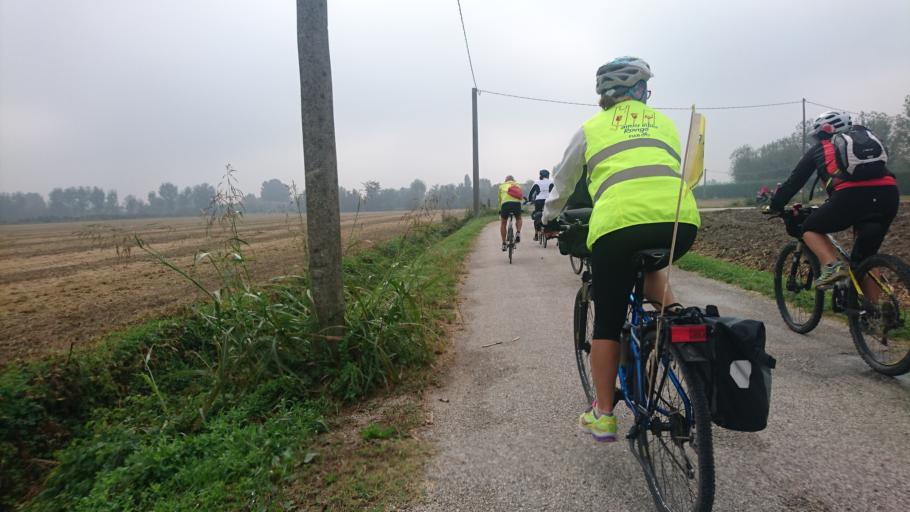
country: IT
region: Veneto
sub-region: Provincia di Padova
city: Stanghella
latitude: 45.1521
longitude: 11.7836
